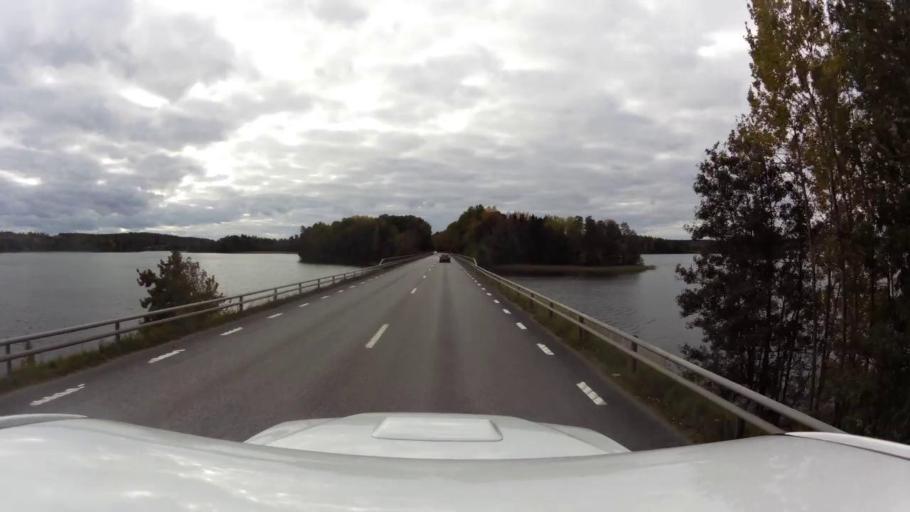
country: SE
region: OEstergoetland
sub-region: Kinda Kommun
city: Rimforsa
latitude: 58.1693
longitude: 15.6774
